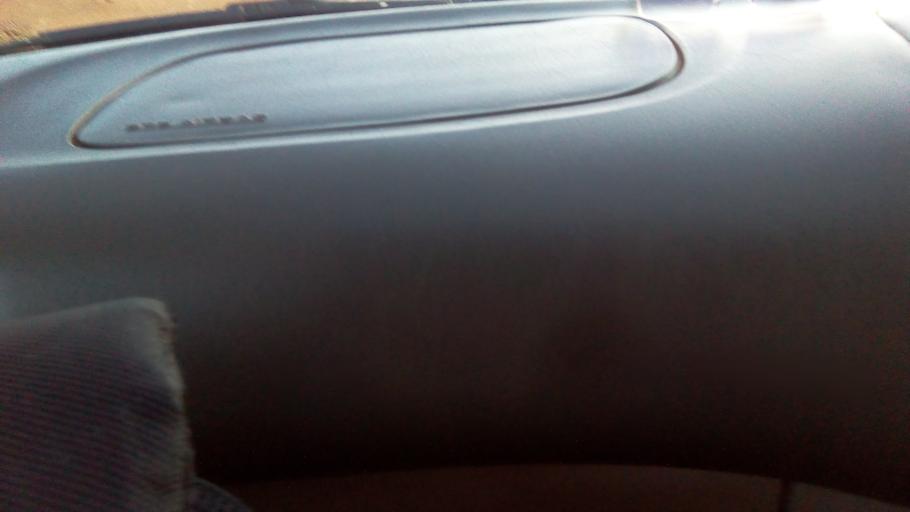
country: ZM
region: Lusaka
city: Lusaka
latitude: -15.4500
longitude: 28.3480
